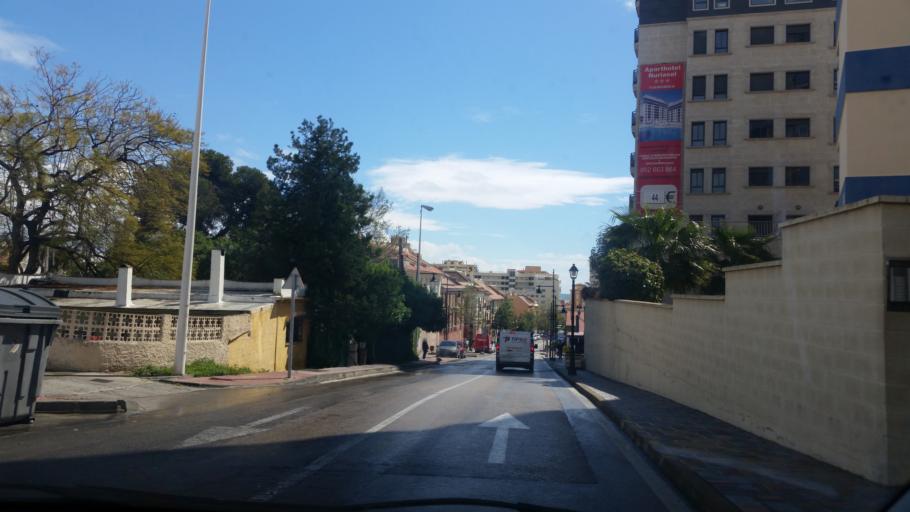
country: ES
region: Andalusia
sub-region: Provincia de Malaga
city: Fuengirola
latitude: 36.5571
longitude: -4.6175
